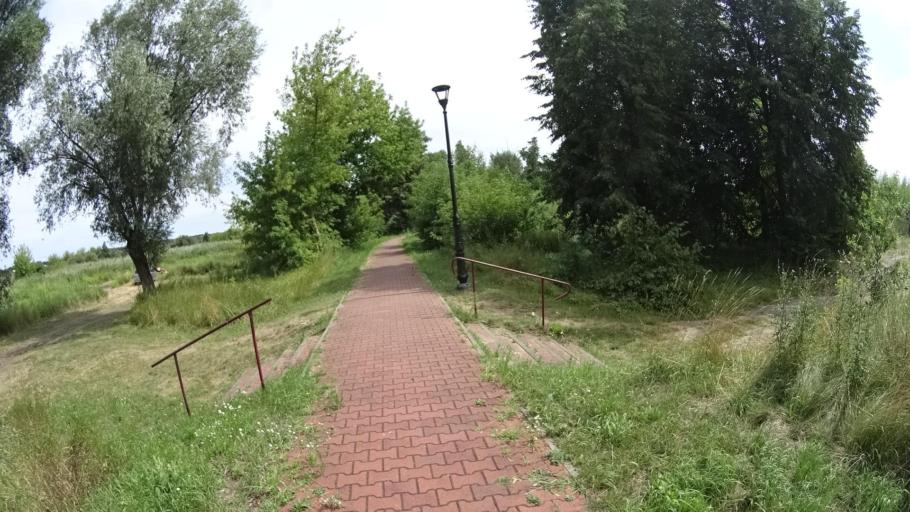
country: PL
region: Masovian Voivodeship
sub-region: Powiat bialobrzeski
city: Bialobrzegi
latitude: 51.6566
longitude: 20.9522
